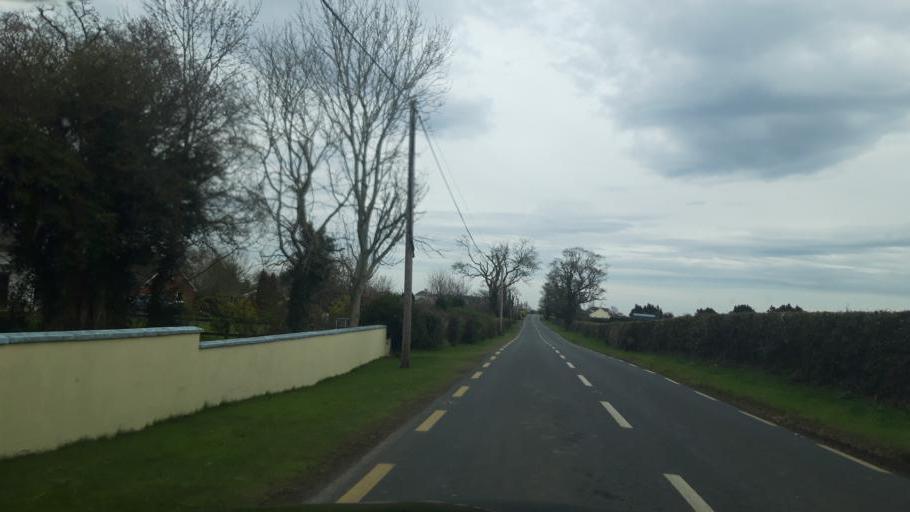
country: IE
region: Leinster
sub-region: Kildare
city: Clane
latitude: 53.3367
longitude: -6.6704
